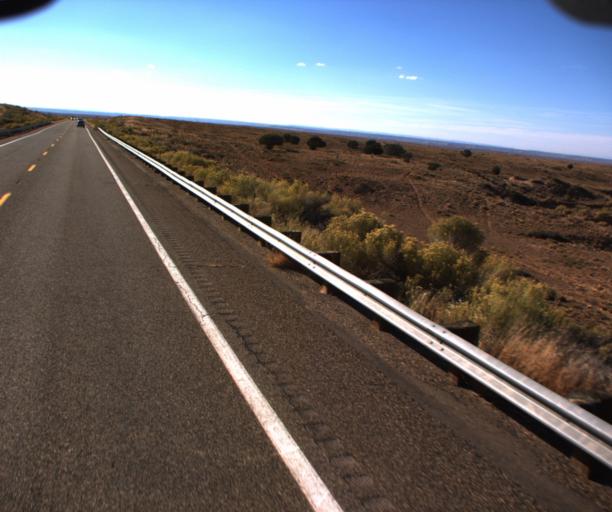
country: US
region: Arizona
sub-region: Coconino County
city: Kaibito
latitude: 36.6148
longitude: -110.9939
